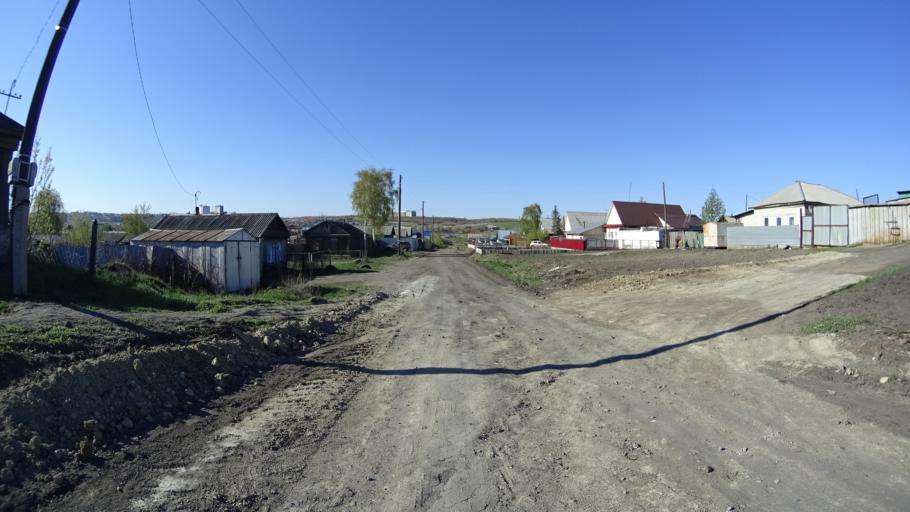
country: RU
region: Chelyabinsk
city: Troitsk
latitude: 54.0904
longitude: 61.6000
